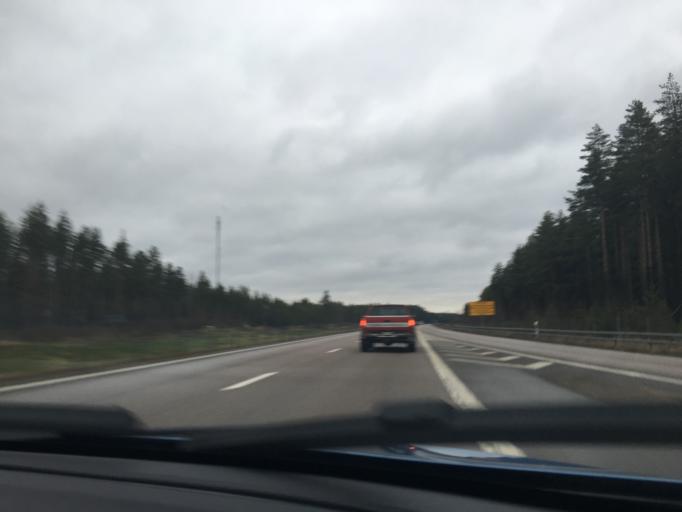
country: SE
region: Uppsala
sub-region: Alvkarleby Kommun
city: AElvkarleby
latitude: 60.4407
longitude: 17.4202
